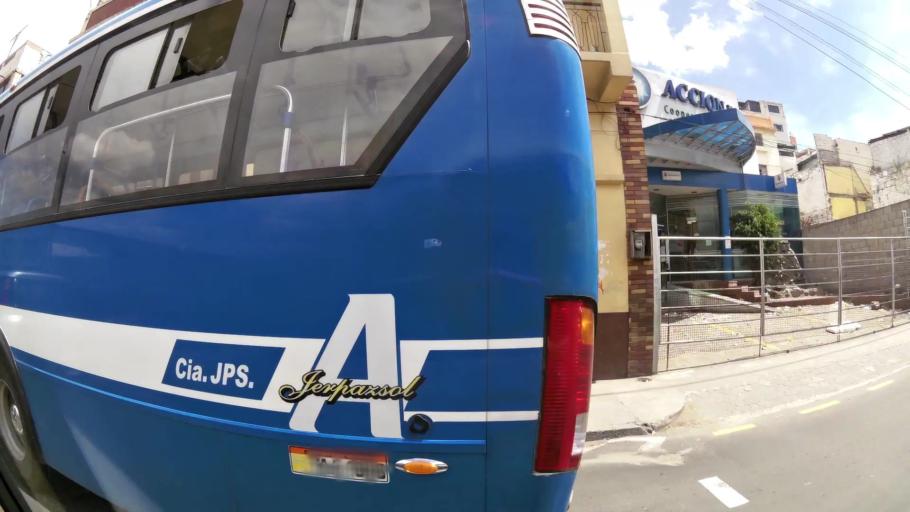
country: EC
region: Tungurahua
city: Ambato
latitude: -1.2378
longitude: -78.6219
